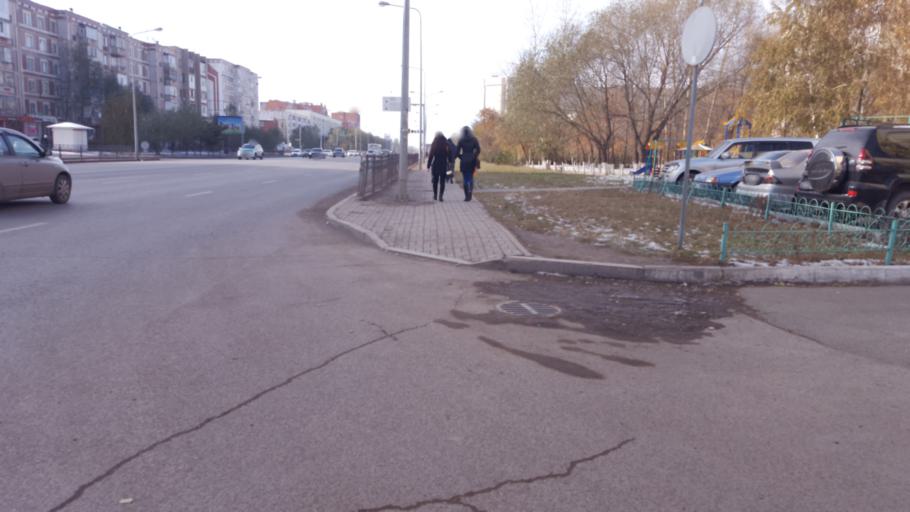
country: KZ
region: Astana Qalasy
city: Astana
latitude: 51.1568
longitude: 71.4752
